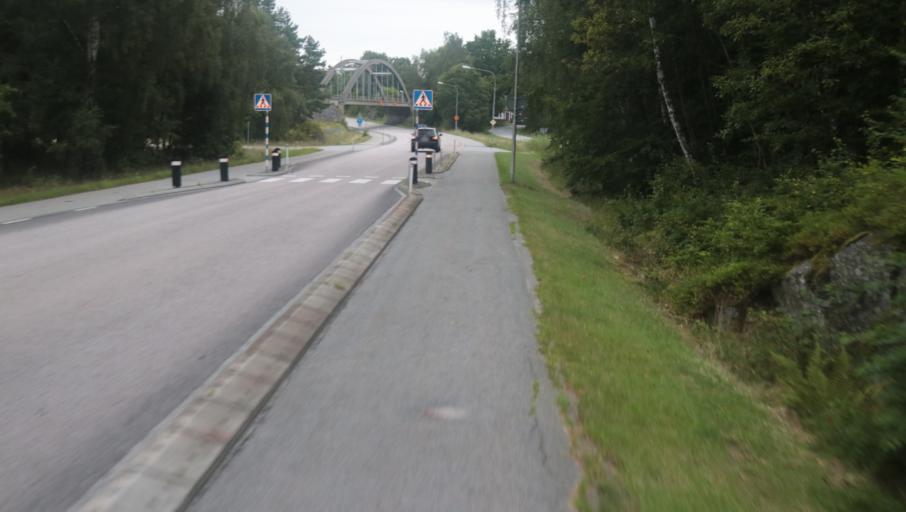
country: SE
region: Blekinge
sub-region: Karlshamns Kommun
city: Karlshamn
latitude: 56.1717
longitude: 14.8969
